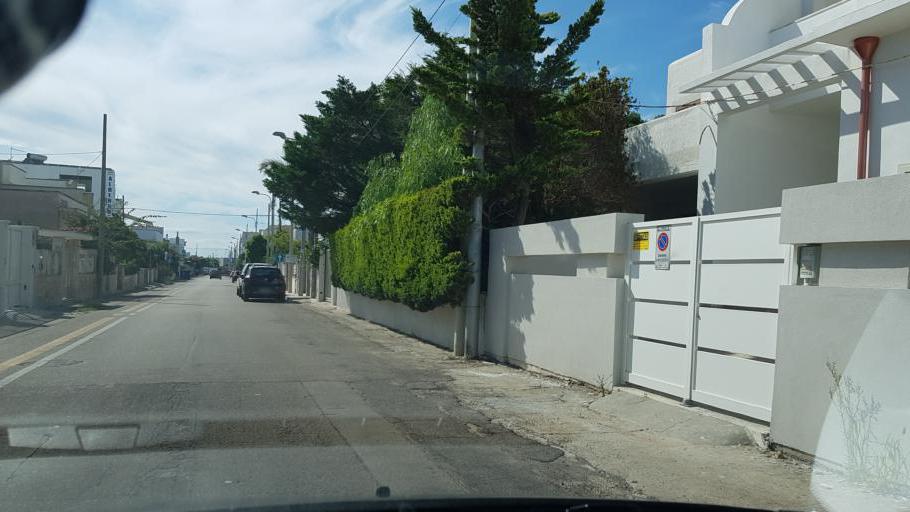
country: IT
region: Apulia
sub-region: Provincia di Lecce
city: Borgagne
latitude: 40.2762
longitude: 18.4289
